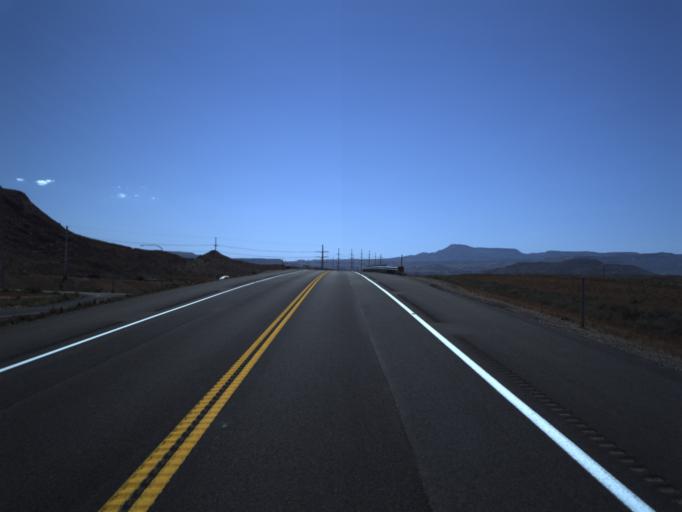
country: US
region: Utah
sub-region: Washington County
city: Washington
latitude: 37.0612
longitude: -113.4861
